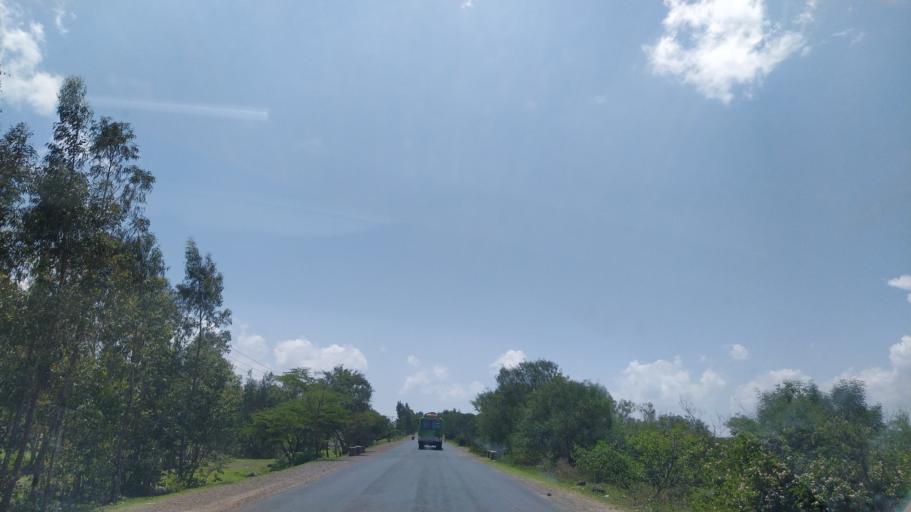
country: ET
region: Southern Nations, Nationalities, and People's Region
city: Butajira
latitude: 7.7832
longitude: 38.1404
